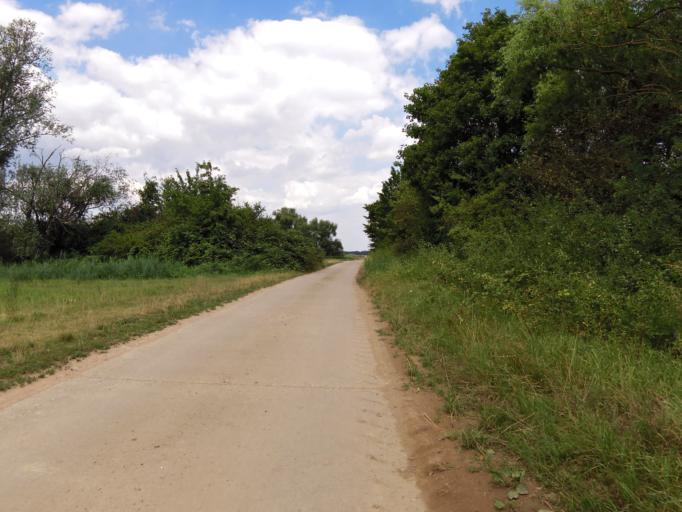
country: DE
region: Rheinland-Pfalz
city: Fussgonheim
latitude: 49.4521
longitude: 8.2814
